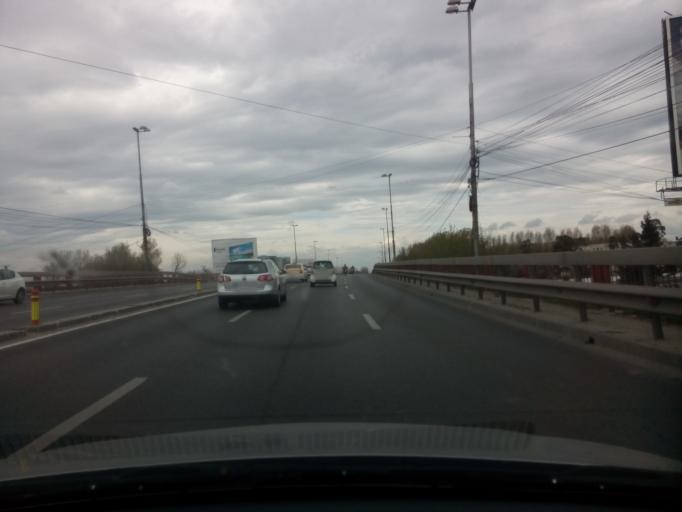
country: RO
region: Ilfov
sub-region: Comuna Otopeni
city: Otopeni
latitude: 44.5335
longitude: 26.0685
